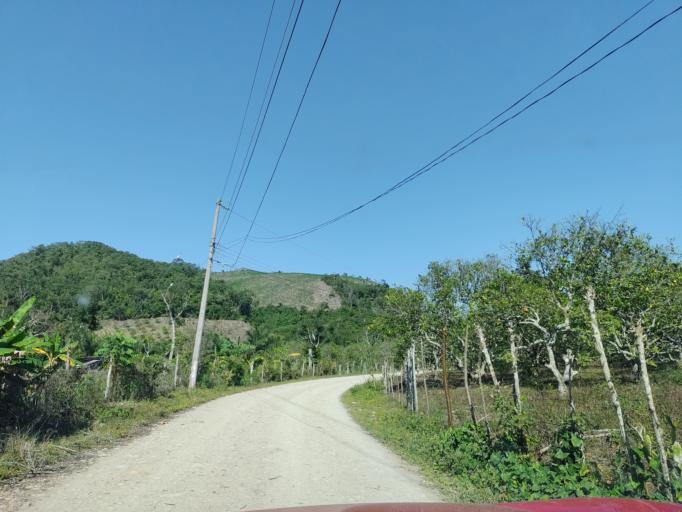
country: MX
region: Veracruz
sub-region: Papantla
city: Polutla
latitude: 20.4913
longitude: -97.1838
